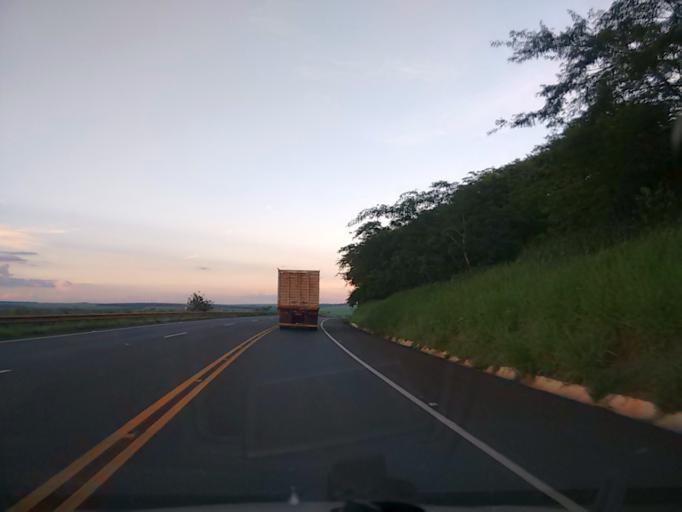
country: BR
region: Sao Paulo
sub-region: Boa Esperanca Do Sul
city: Boa Esperanca do Sul
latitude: -22.0955
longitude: -48.4525
